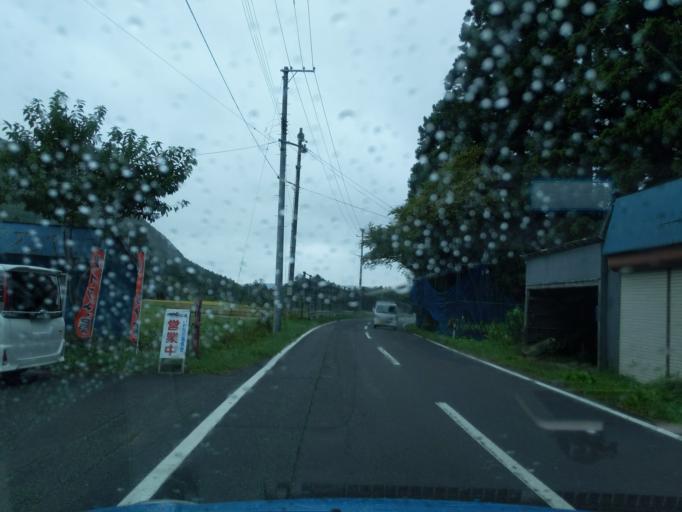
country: JP
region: Iwate
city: Ichinoseki
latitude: 38.9979
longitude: 140.8988
